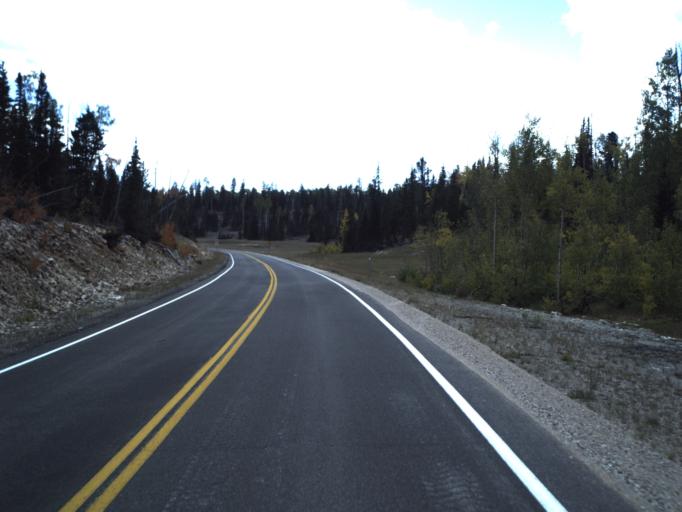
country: US
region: Utah
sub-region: Iron County
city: Parowan
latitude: 37.5460
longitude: -112.7858
